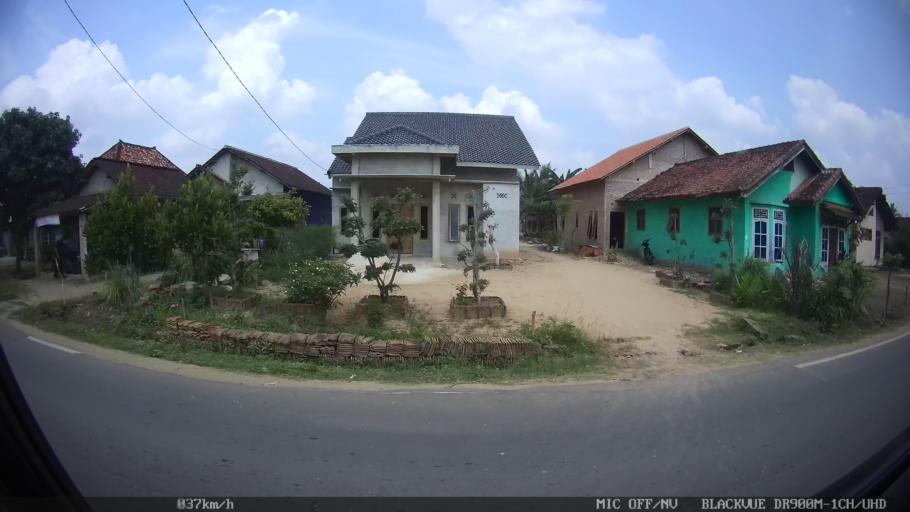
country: ID
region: Lampung
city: Pringsewu
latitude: -5.3748
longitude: 104.9662
